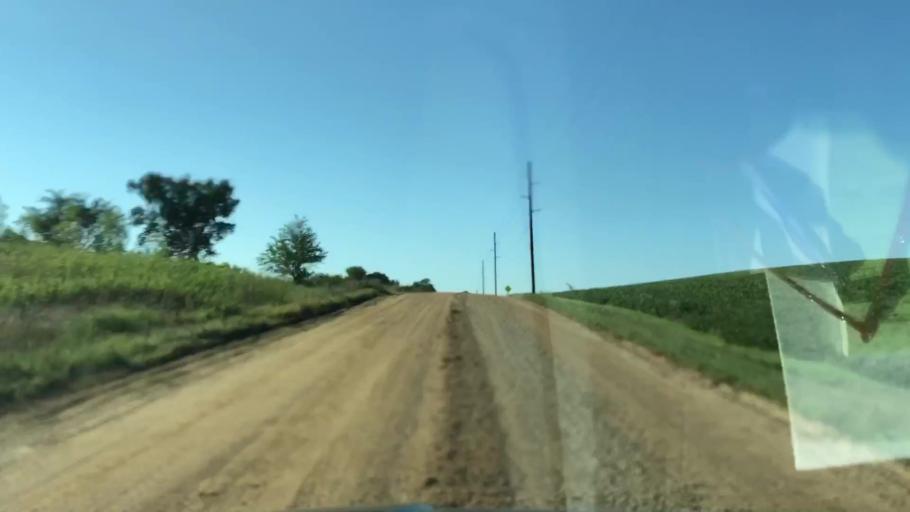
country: US
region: Iowa
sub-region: Woodbury County
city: Sergeant Bluff
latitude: 42.4594
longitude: -96.2527
